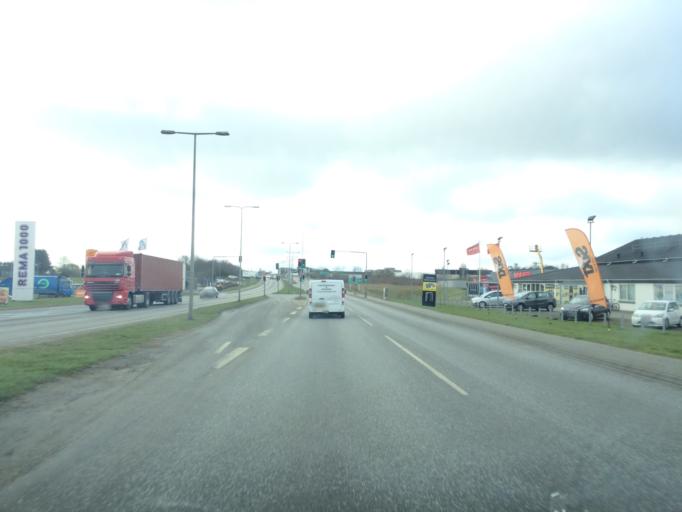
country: DK
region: South Denmark
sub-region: Fredericia Kommune
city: Snoghoj
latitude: 55.5369
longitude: 9.7164
